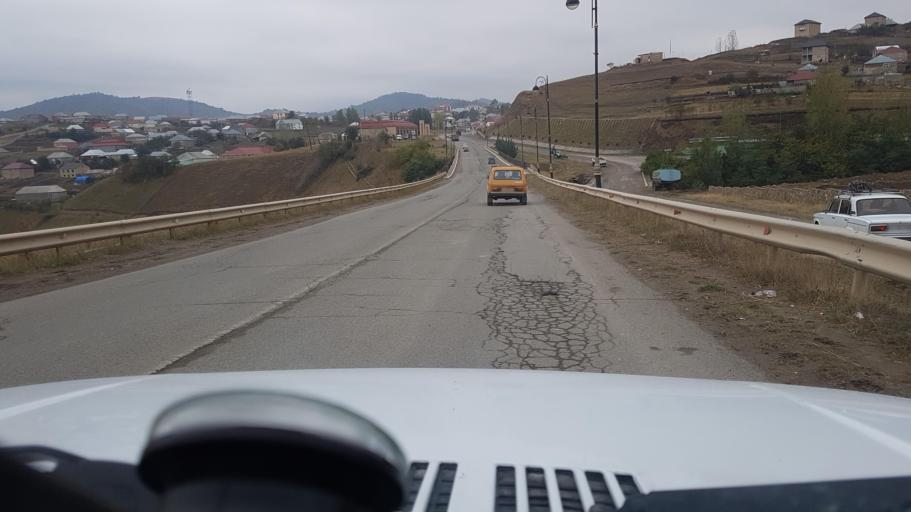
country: AZ
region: Gadabay Rayon
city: Ariqdam
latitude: 40.5874
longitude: 45.8109
